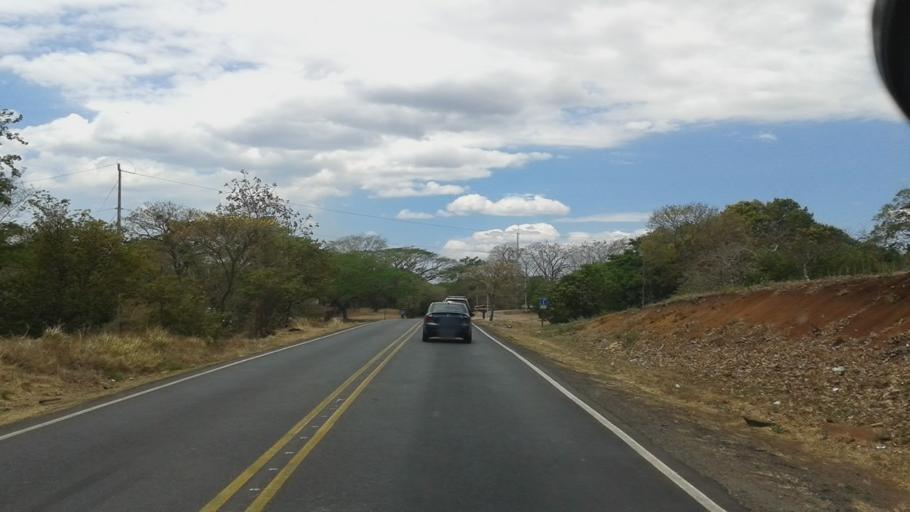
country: CR
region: Puntarenas
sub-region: Canton Central de Puntarenas
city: Puntarenas
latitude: 10.0989
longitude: -84.8653
